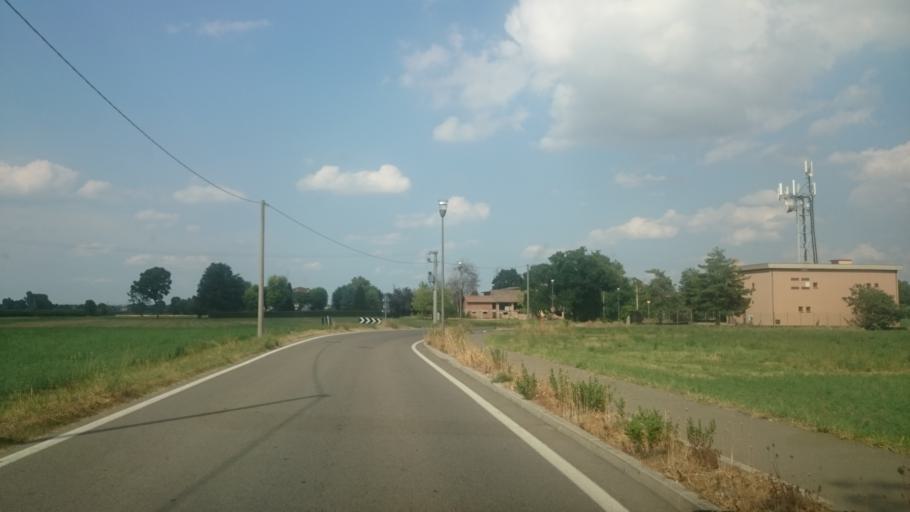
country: IT
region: Emilia-Romagna
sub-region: Provincia di Reggio Emilia
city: Casalgrande
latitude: 44.5884
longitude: 10.7478
